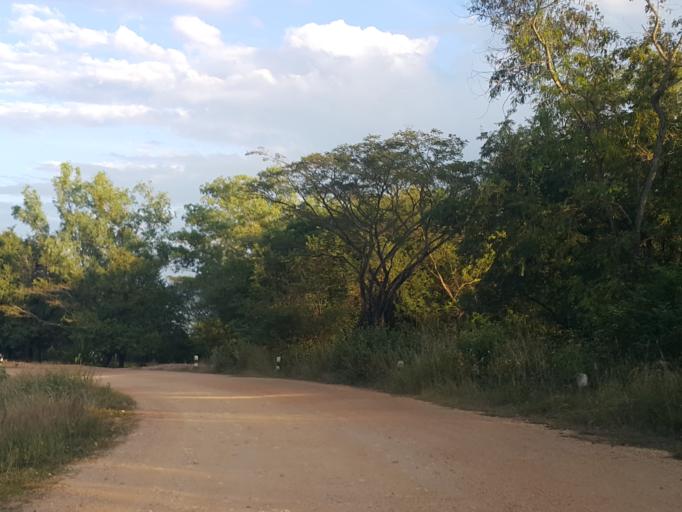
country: TH
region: Lampang
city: Mae Mo
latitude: 18.4333
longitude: 99.6018
